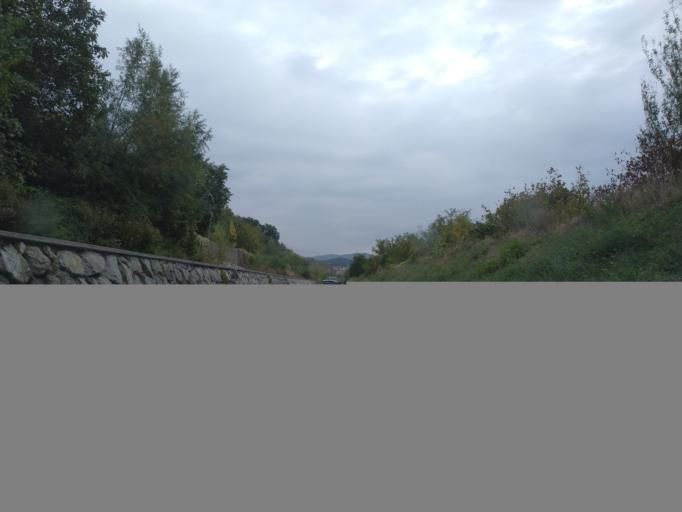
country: SI
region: Nova Gorica
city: Solkan
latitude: 45.9689
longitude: 13.6526
